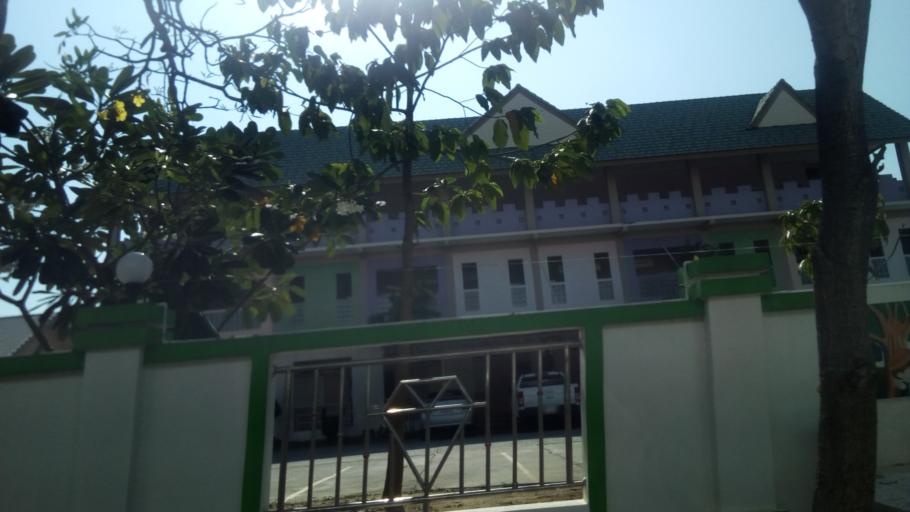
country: TH
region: Nakhon Pathom
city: Salaya
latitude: 13.8118
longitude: 100.3091
